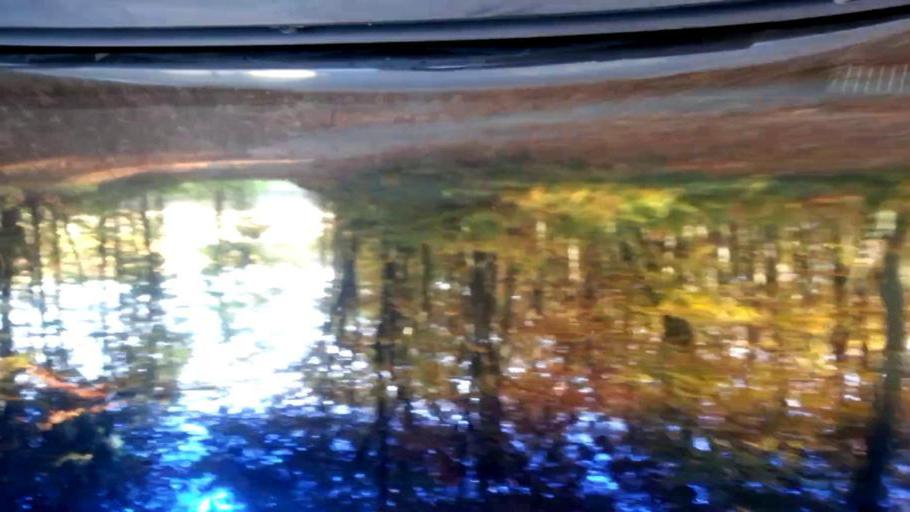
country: DE
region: Bavaria
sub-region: Upper Franconia
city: Heiligenstadt
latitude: 49.8624
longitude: 11.1831
